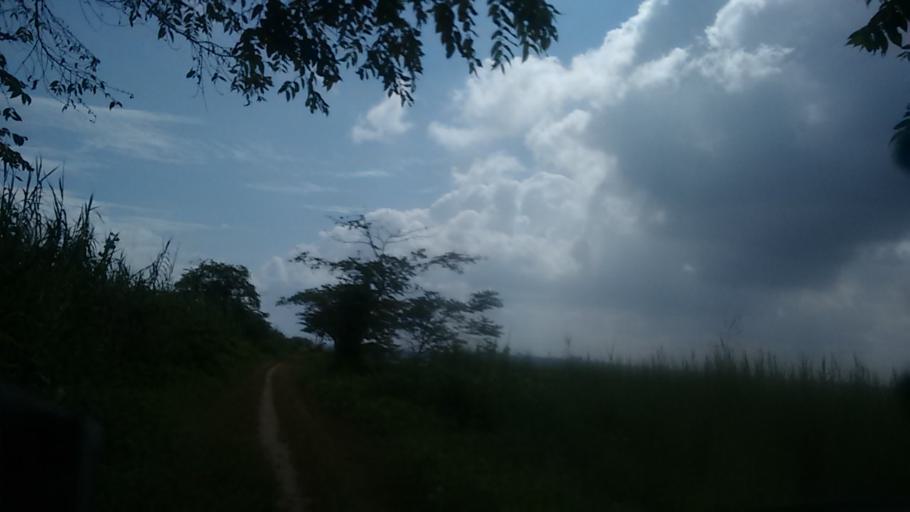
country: IN
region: Kerala
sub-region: Thrissur District
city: Trichur
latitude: 10.5305
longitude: 76.1477
